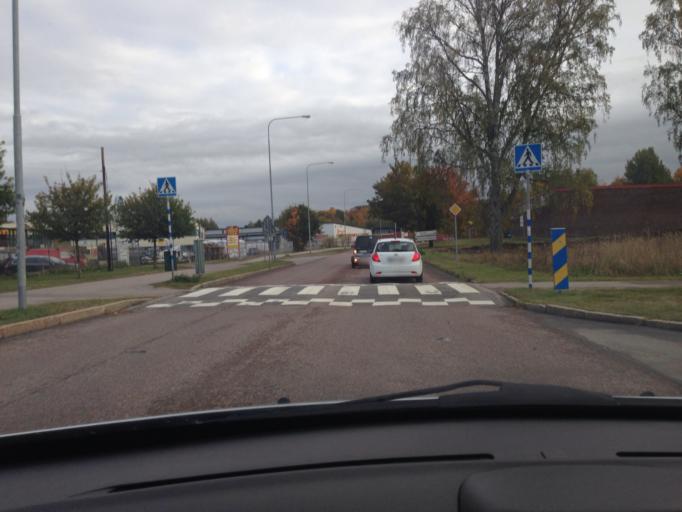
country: SE
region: Gaevleborg
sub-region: Gavle Kommun
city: Gavle
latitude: 60.6769
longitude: 17.1804
